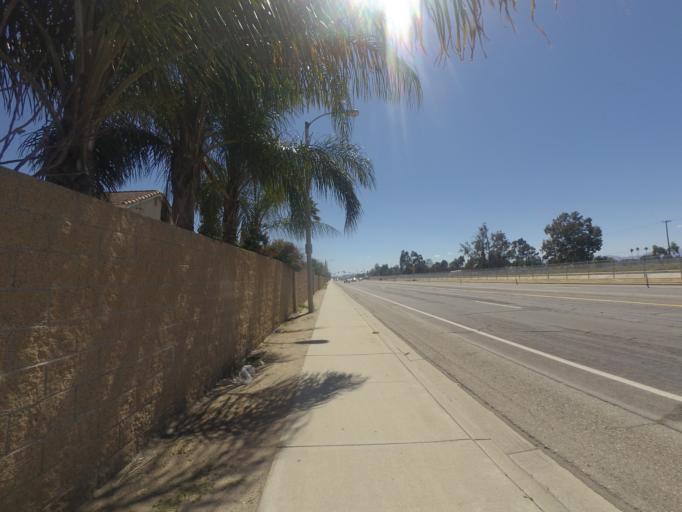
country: US
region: California
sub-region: Riverside County
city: March Air Force Base
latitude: 33.9052
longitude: -117.2435
